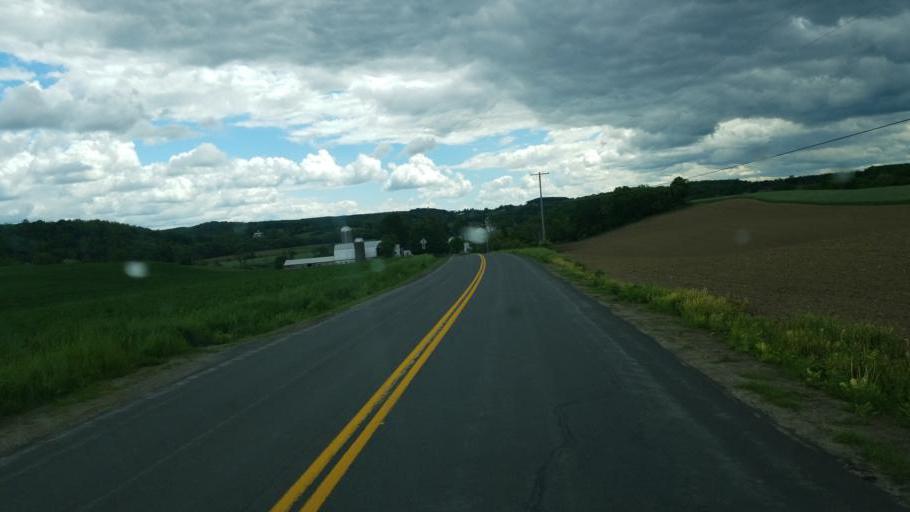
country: US
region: New York
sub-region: Oneida County
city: Chadwicks
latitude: 42.9318
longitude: -75.1981
